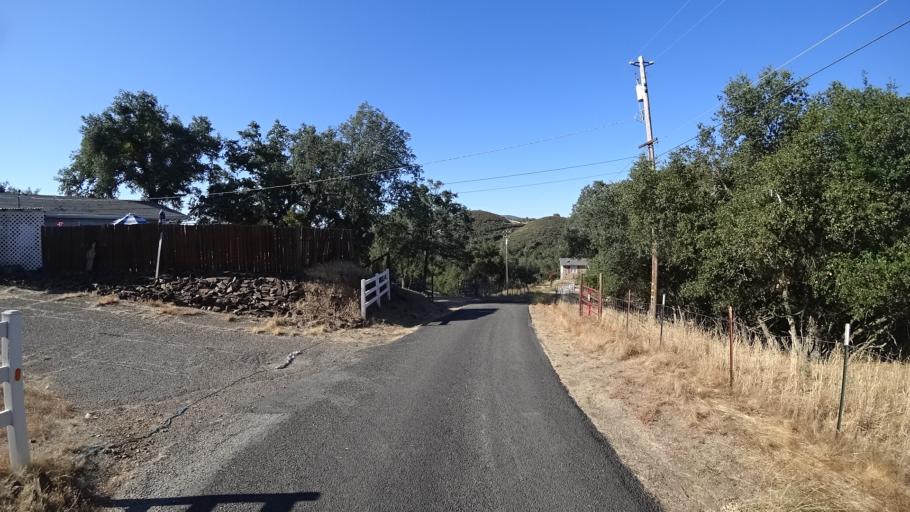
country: US
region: California
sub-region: Calaveras County
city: San Andreas
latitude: 38.2294
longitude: -120.7127
